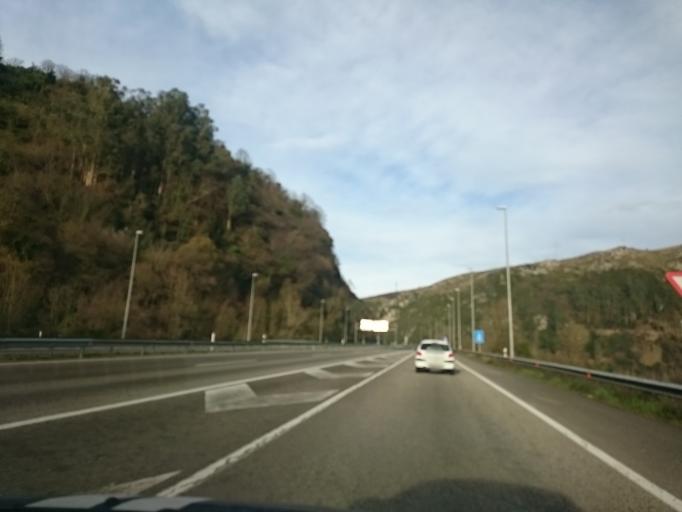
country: ES
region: Asturias
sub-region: Province of Asturias
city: Castandiello
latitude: 43.3012
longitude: -5.8431
